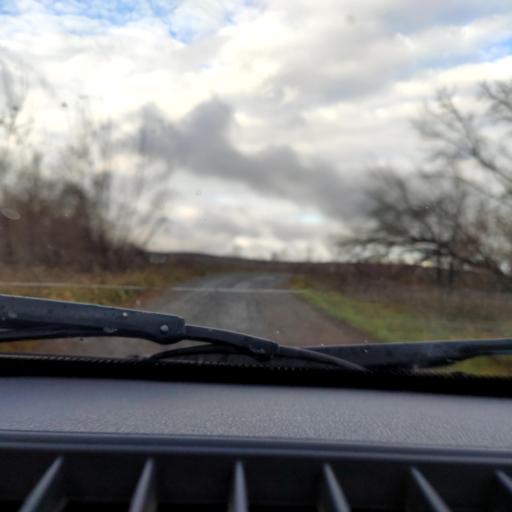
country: RU
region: Bashkortostan
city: Avdon
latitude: 54.6345
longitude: 55.7268
